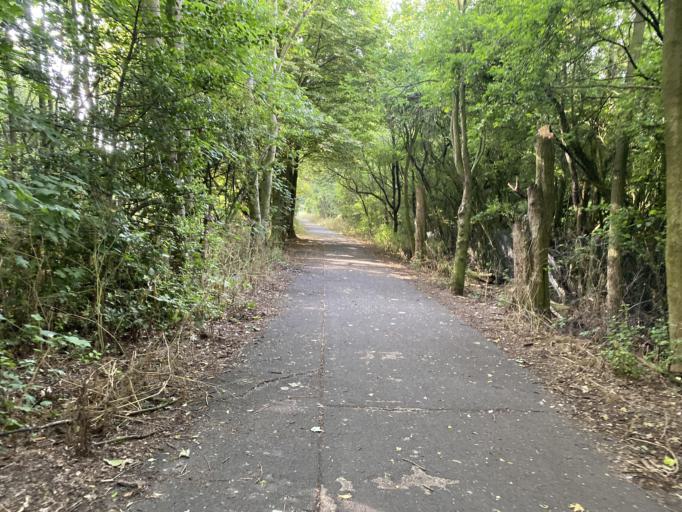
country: GB
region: England
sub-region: Suffolk
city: Haverhill
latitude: 52.0777
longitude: 0.4524
